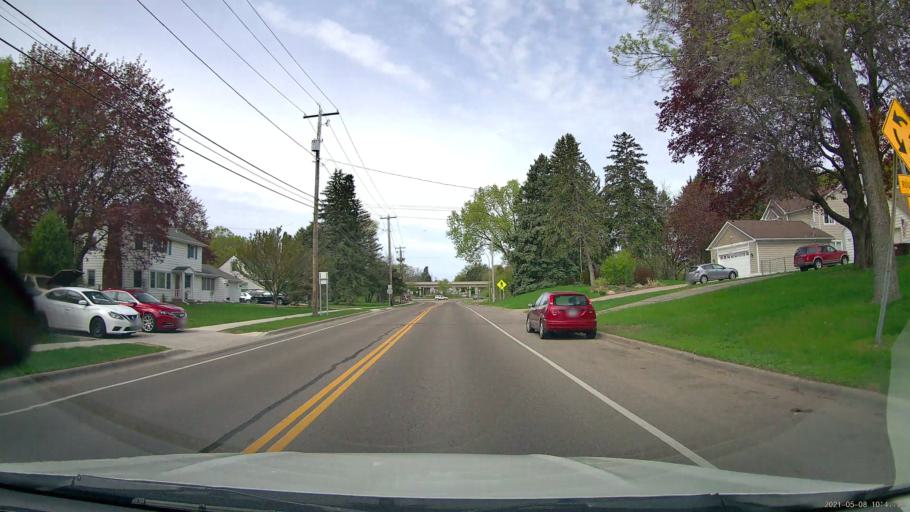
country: US
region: Minnesota
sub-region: Dakota County
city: South Saint Paul
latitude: 44.8980
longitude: -93.0632
